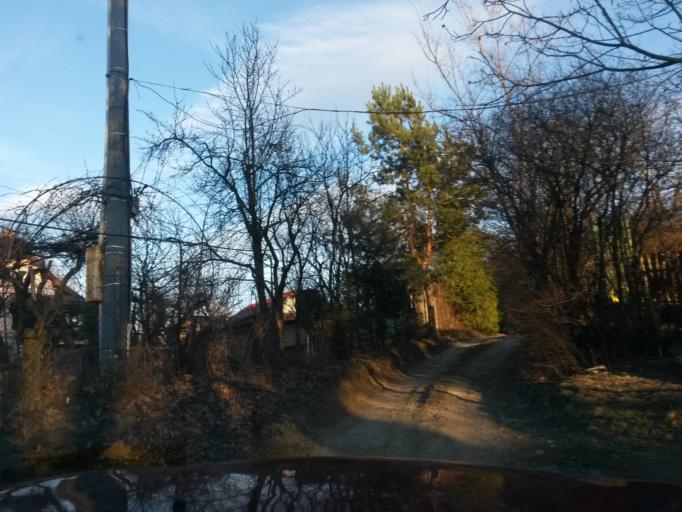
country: SK
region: Kosicky
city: Kosice
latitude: 48.7059
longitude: 21.2939
